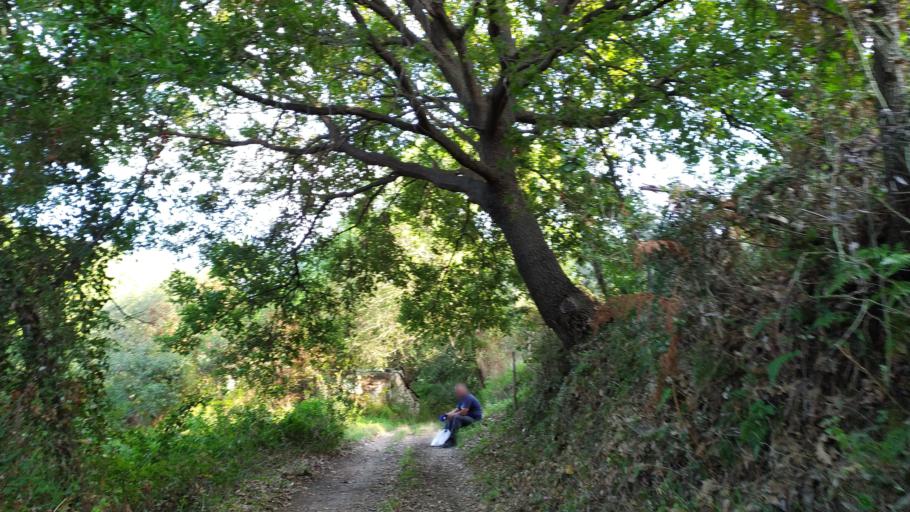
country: IT
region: Sicily
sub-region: Messina
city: Condro
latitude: 38.1626
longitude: 15.3321
